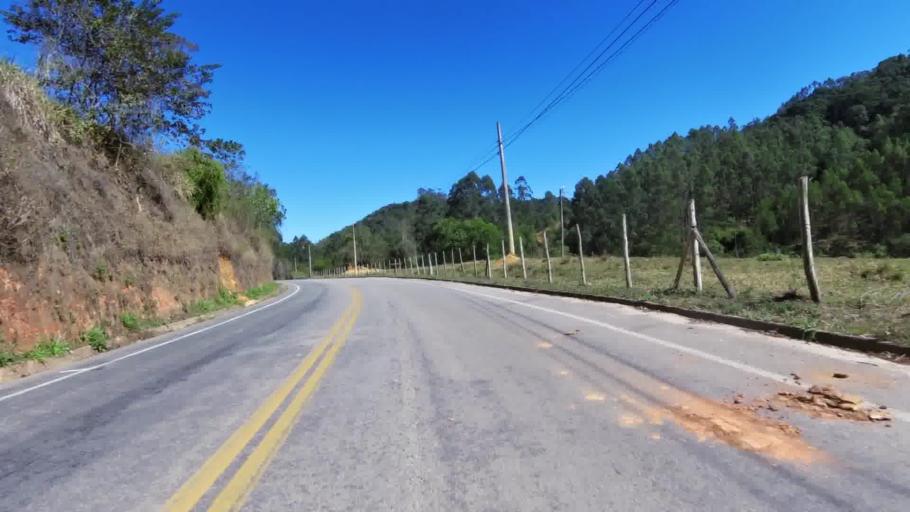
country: BR
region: Espirito Santo
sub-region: Vargem Alta
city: Vargem Alta
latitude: -20.6619
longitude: -40.9822
